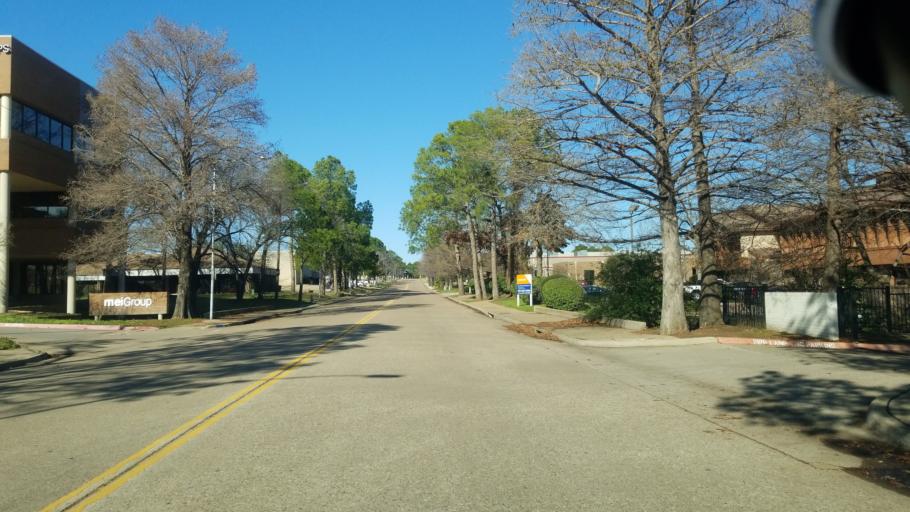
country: US
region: Texas
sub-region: Tarrant County
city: Arlington
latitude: 32.7645
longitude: -97.0679
